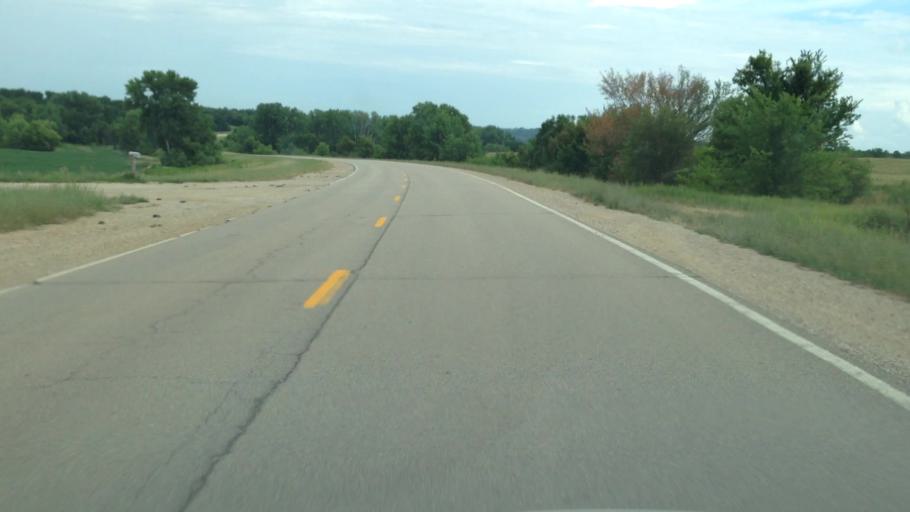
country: US
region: Kansas
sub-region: Shawnee County
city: Topeka
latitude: 39.0978
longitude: -95.4821
